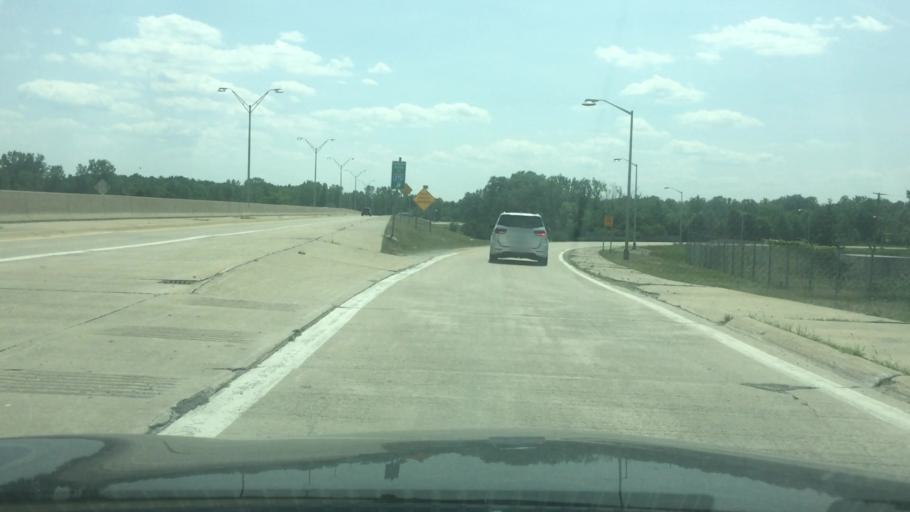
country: US
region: Michigan
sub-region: Wayne County
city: Romulus
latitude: 42.1948
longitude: -83.3639
